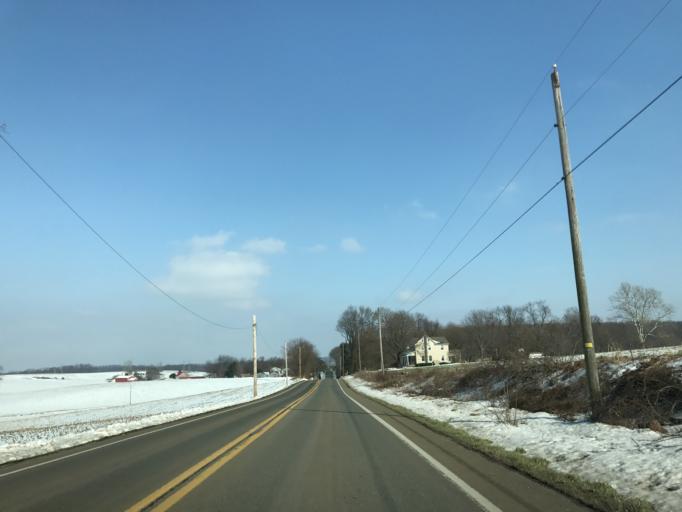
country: US
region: Pennsylvania
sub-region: York County
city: Susquehanna Trails
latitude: 39.7213
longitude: -76.4083
